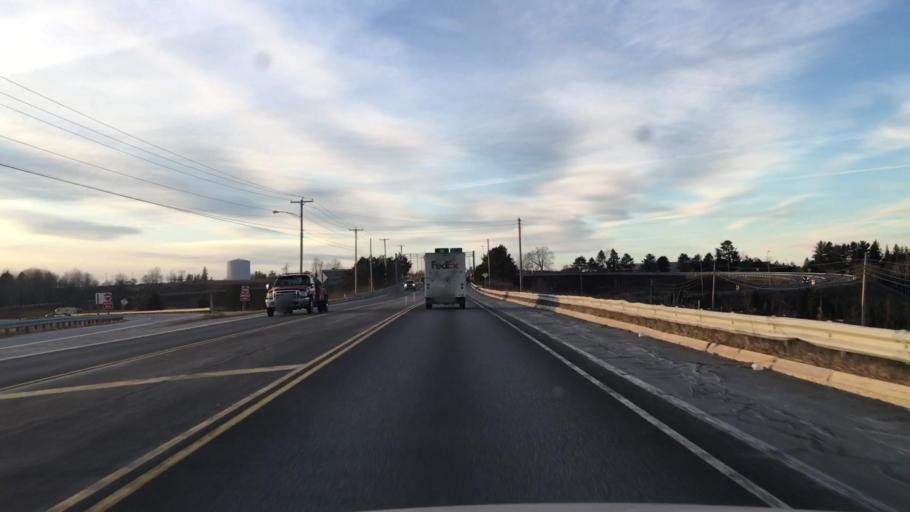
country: US
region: Maine
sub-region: Penobscot County
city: Holden
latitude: 44.7702
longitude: -68.7187
